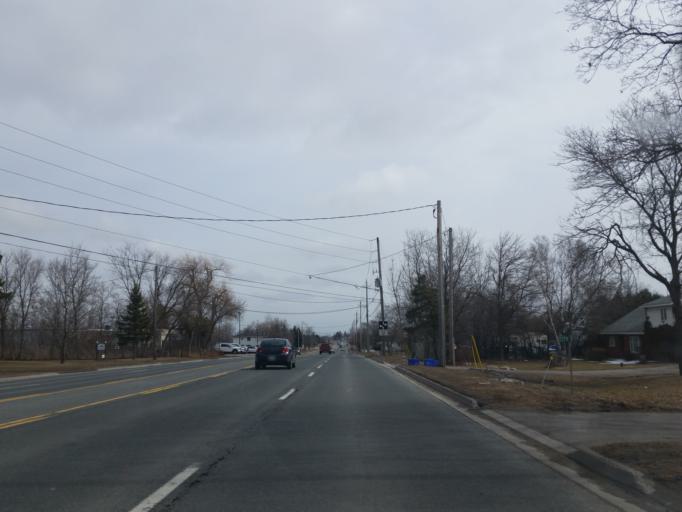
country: CA
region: Ontario
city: Oshawa
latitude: 43.9120
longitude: -78.7321
